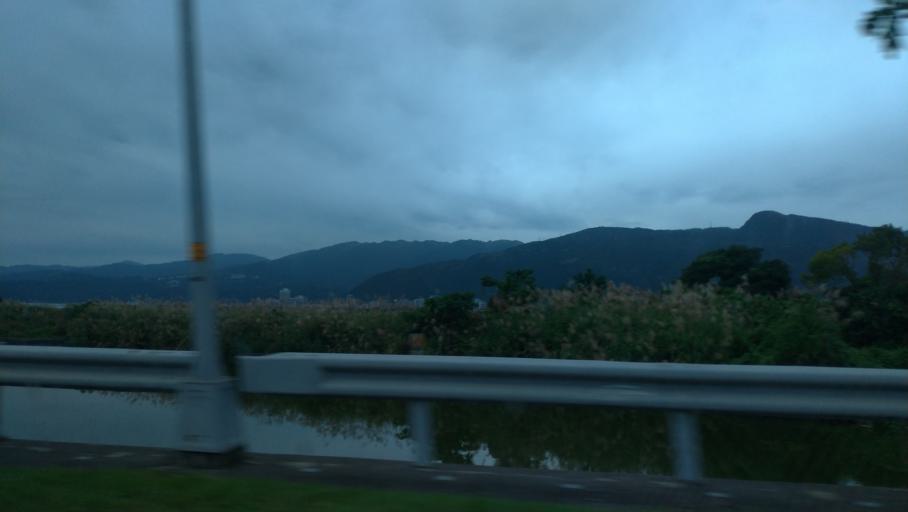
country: TW
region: Taiwan
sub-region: Yilan
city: Yilan
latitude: 24.8240
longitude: 121.7993
